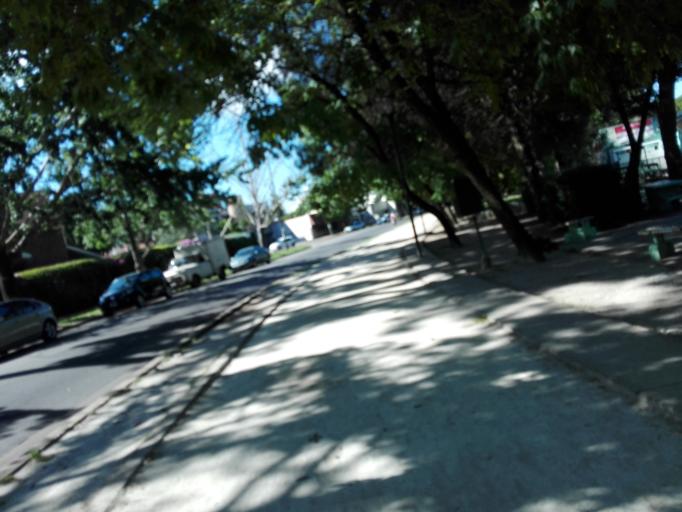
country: AR
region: Buenos Aires
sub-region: Partido de La Plata
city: La Plata
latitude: -34.9337
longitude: -57.9694
